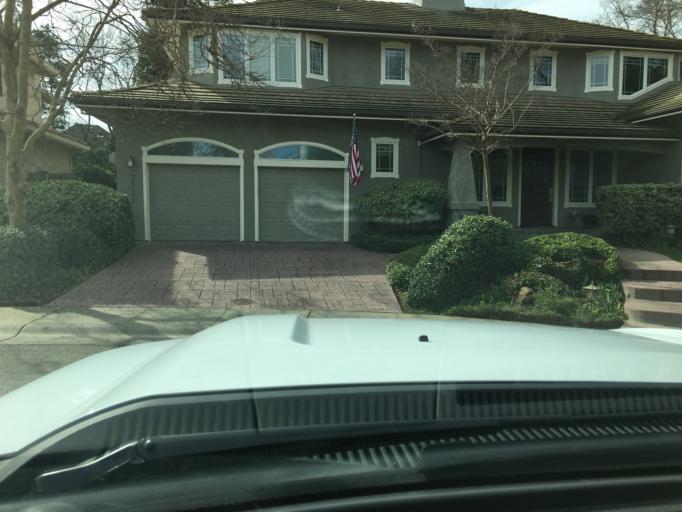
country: US
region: California
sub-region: Yolo County
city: Davis
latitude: 38.5567
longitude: -121.7780
